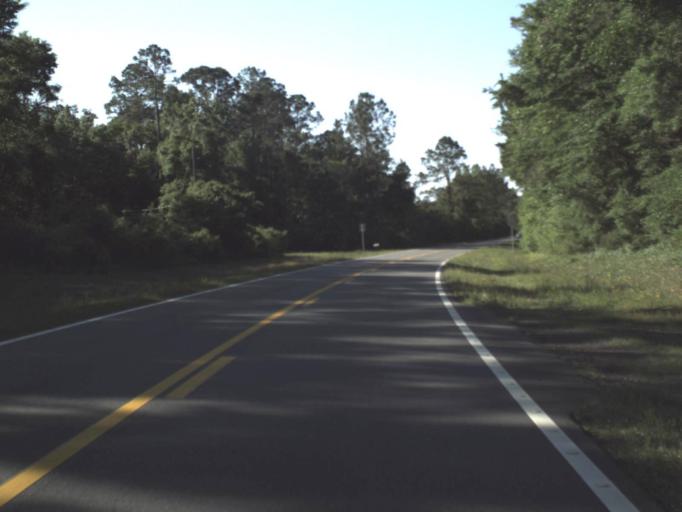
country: US
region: Florida
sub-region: Gulf County
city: Wewahitchka
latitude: 30.0289
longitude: -84.9835
